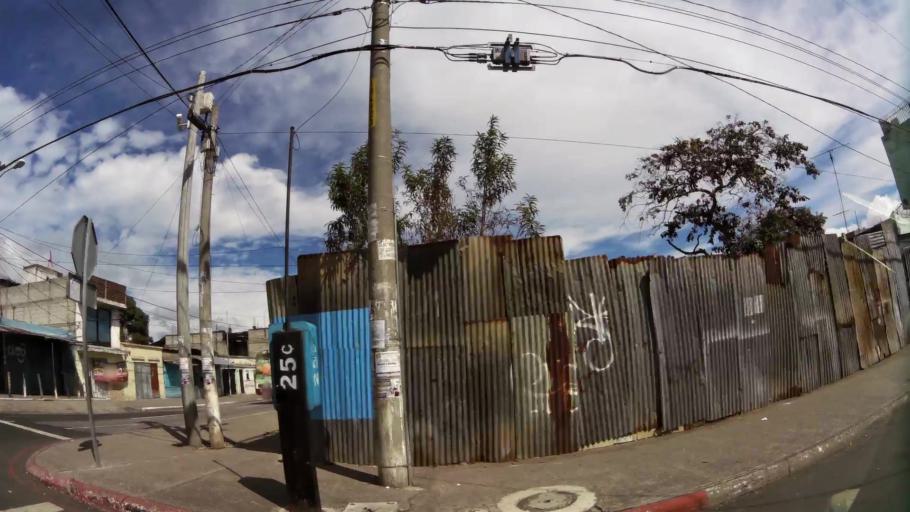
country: GT
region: Guatemala
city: Mixco
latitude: 14.6530
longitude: -90.5841
